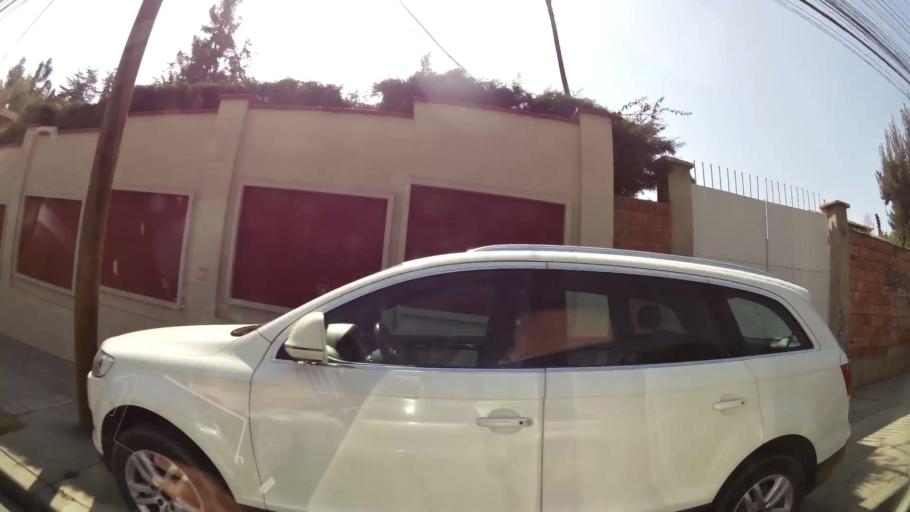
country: BO
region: La Paz
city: La Paz
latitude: -16.5446
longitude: -68.0888
